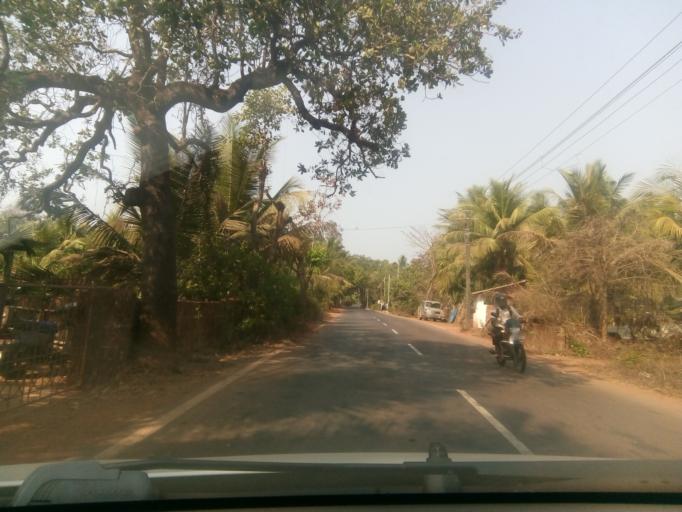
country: IN
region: Goa
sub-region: North Goa
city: Pernem
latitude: 15.6961
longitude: 73.8452
